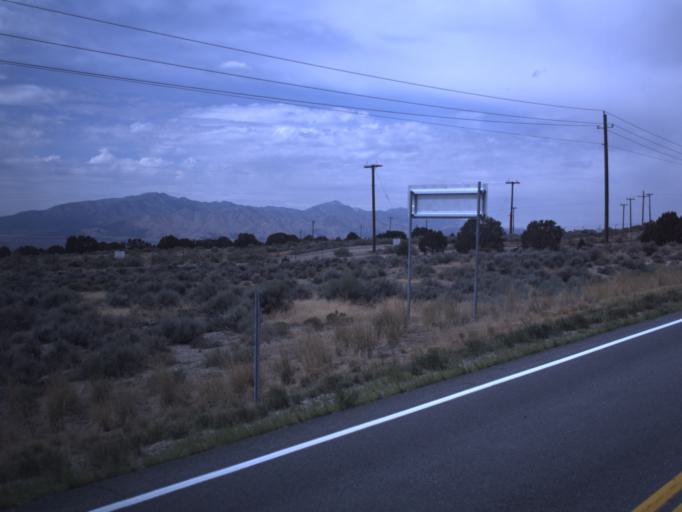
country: US
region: Utah
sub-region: Tooele County
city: Tooele
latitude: 40.3252
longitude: -112.2887
